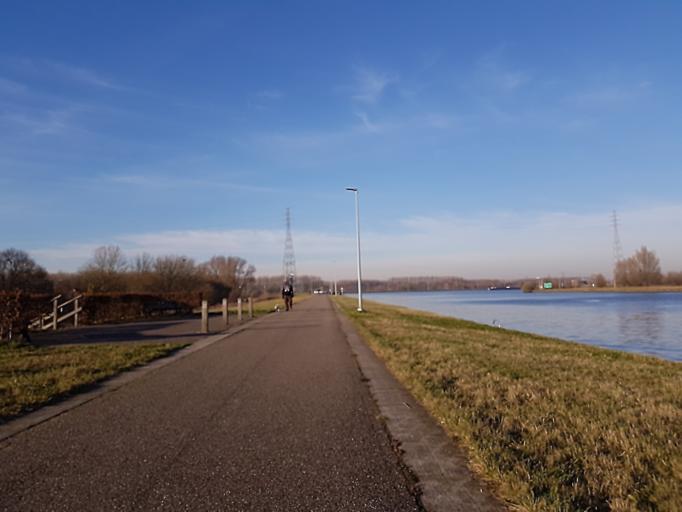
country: BE
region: Flanders
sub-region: Provincie Antwerpen
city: Niel
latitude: 51.1072
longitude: 4.3029
